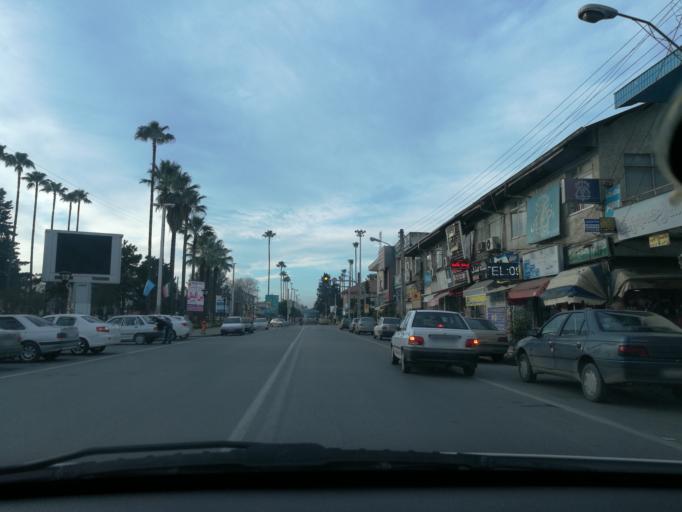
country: IR
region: Mazandaran
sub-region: Nowshahr
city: Nowshahr
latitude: 36.6517
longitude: 51.5029
